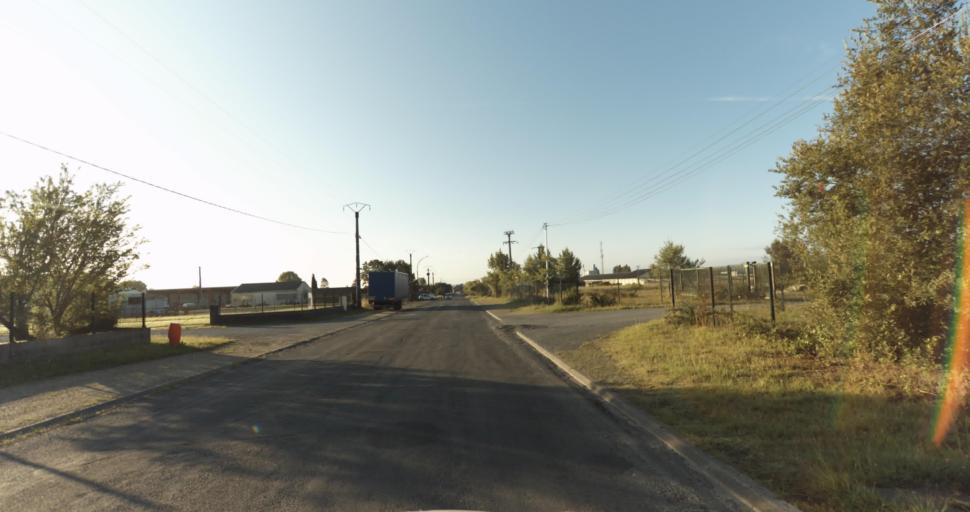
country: FR
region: Aquitaine
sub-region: Departement de la Gironde
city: Bazas
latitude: 44.4402
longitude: -0.2337
